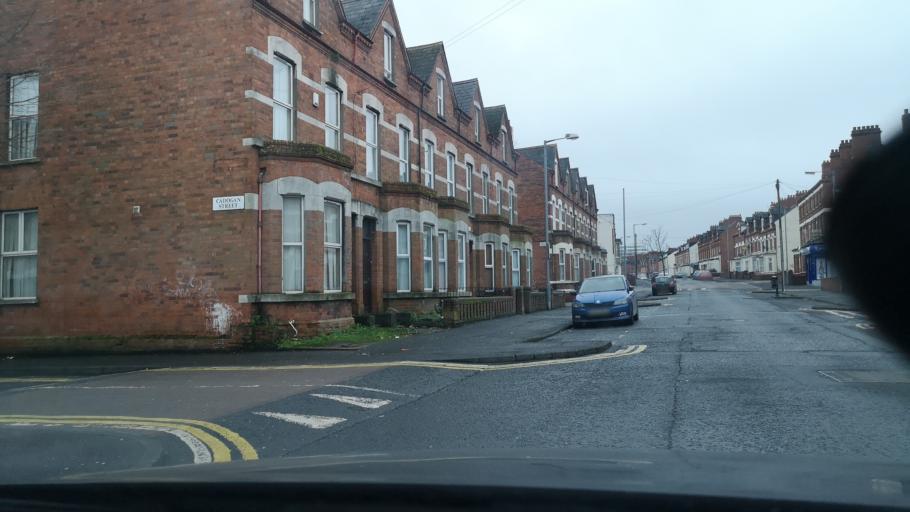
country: GB
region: Northern Ireland
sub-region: City of Belfast
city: Belfast
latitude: 54.5839
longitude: -5.9236
